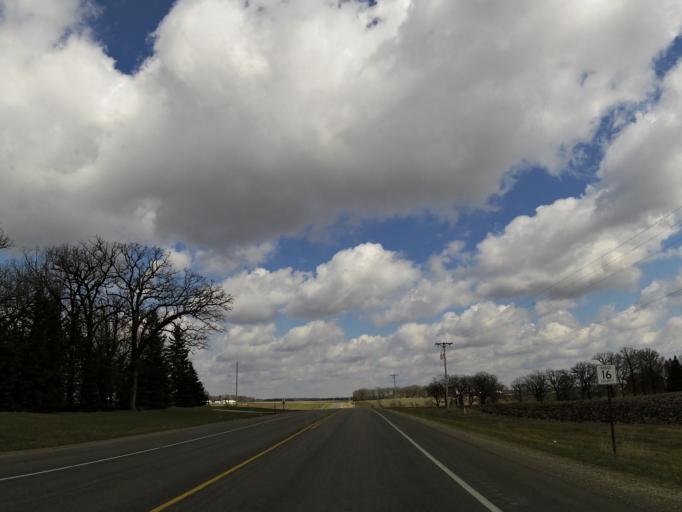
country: US
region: Minnesota
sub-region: Dodge County
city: Mantorville
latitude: 44.0799
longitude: -92.7481
